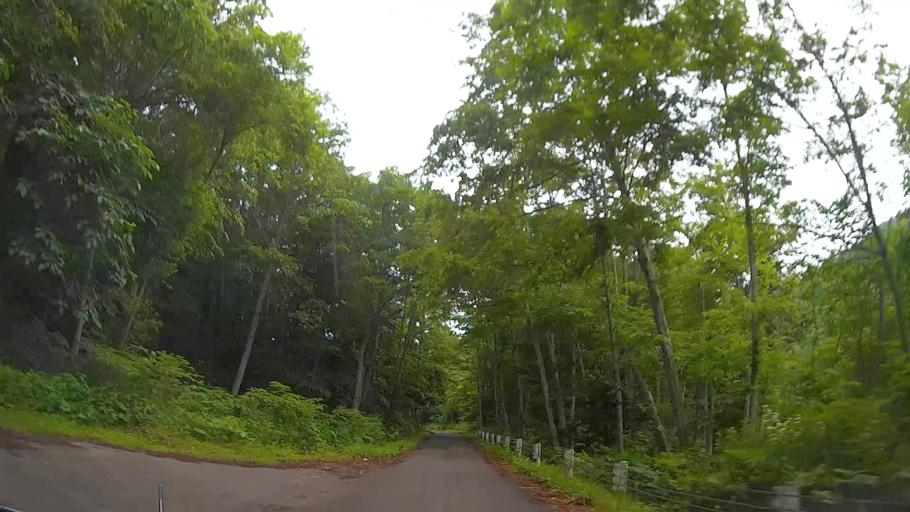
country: JP
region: Hokkaido
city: Nanae
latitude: 42.0585
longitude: 140.5013
